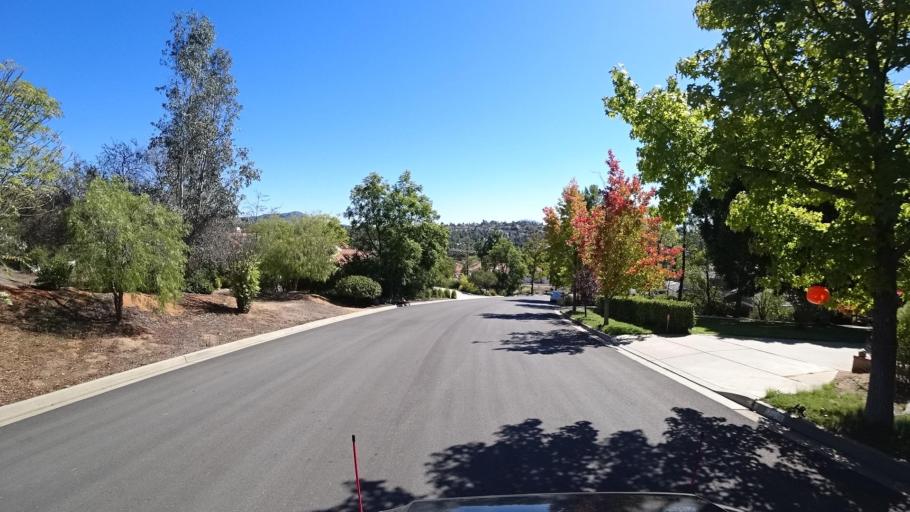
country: US
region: California
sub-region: San Diego County
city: Alpine
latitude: 32.8411
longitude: -116.7640
